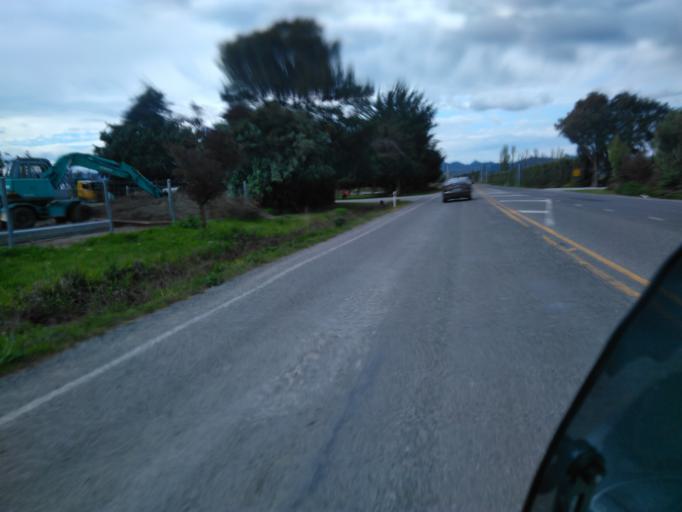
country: NZ
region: Gisborne
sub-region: Gisborne District
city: Gisborne
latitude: -38.6571
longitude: 177.9482
